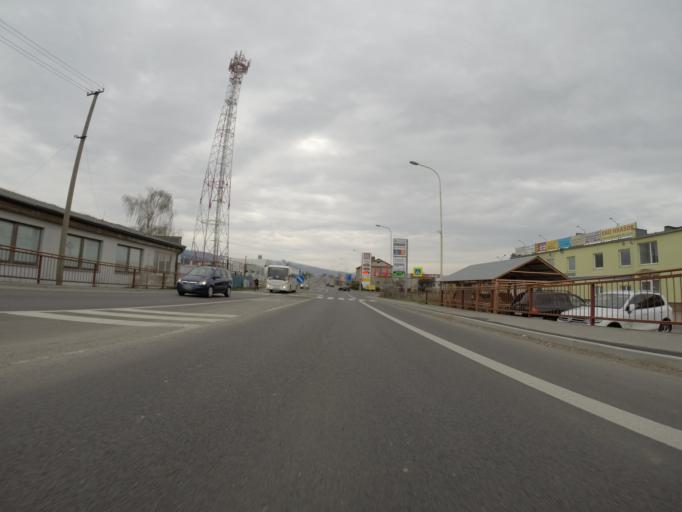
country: SK
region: Nitriansky
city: Prievidza
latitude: 48.7647
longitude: 18.6246
